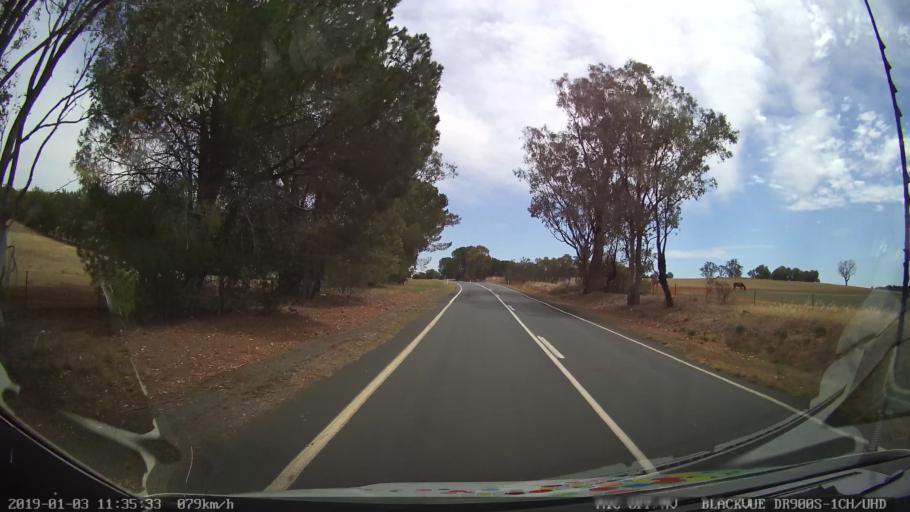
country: AU
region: New South Wales
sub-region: Weddin
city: Grenfell
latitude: -33.9208
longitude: 148.1597
